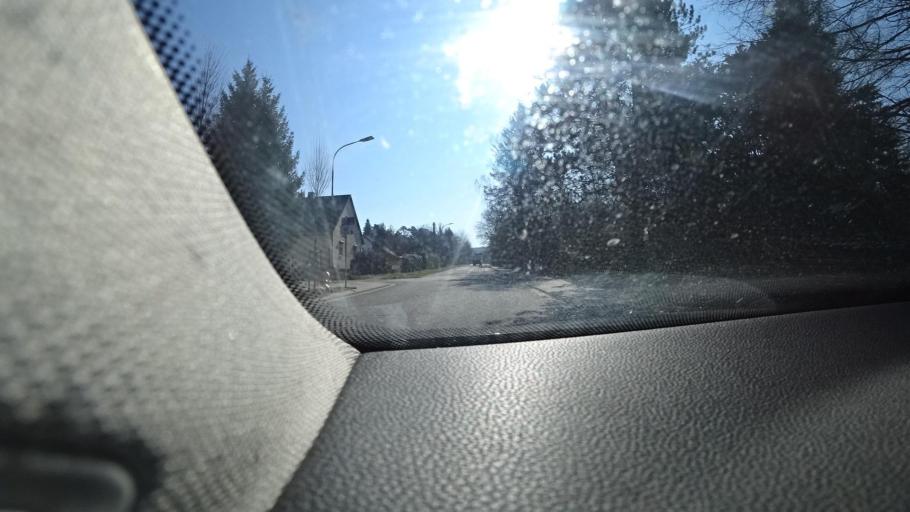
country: DE
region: Rheinland-Pfalz
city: Argenthal
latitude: 49.9686
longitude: 7.6015
